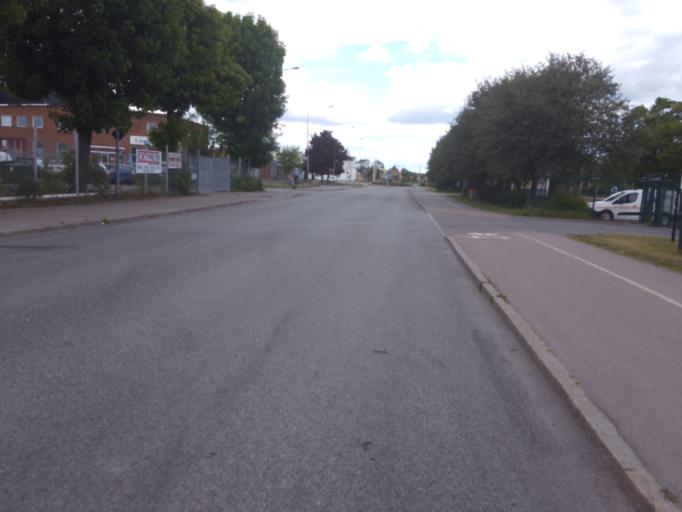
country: SE
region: Uppsala
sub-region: Uppsala Kommun
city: Uppsala
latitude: 59.8544
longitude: 17.6654
